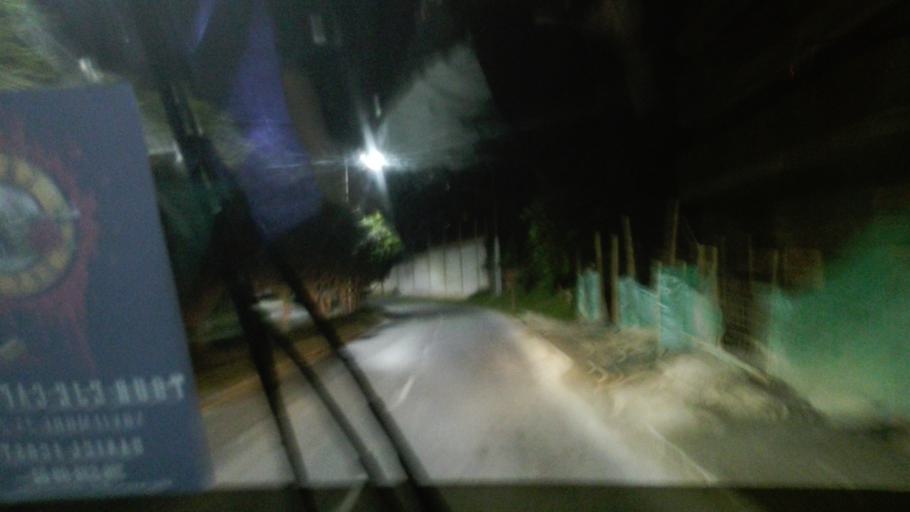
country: CO
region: Quindio
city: Armenia
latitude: 4.5580
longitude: -75.6604
